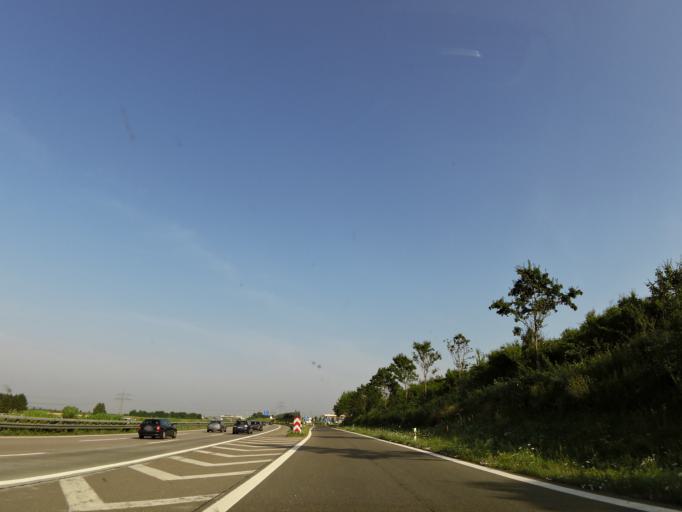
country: DE
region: Baden-Wuerttemberg
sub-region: Regierungsbezirk Stuttgart
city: Denkendorf
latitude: 48.6915
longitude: 9.3089
